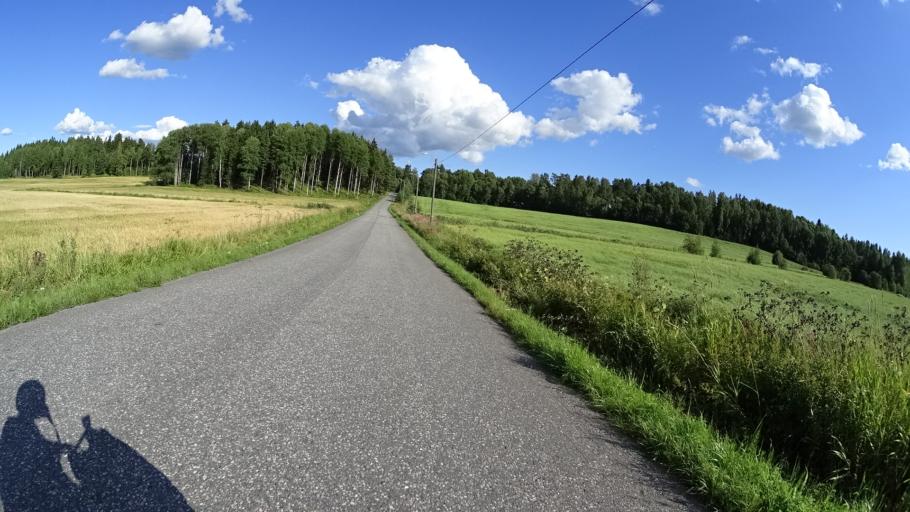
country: FI
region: Uusimaa
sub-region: Helsinki
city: Kilo
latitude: 60.2614
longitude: 24.7729
